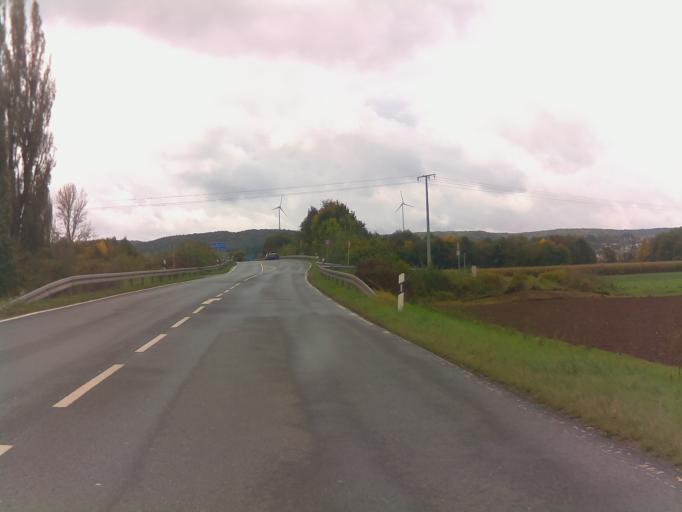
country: DE
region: Bavaria
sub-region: Upper Franconia
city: Viereth-Trunstadt
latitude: 49.9340
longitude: 10.7833
